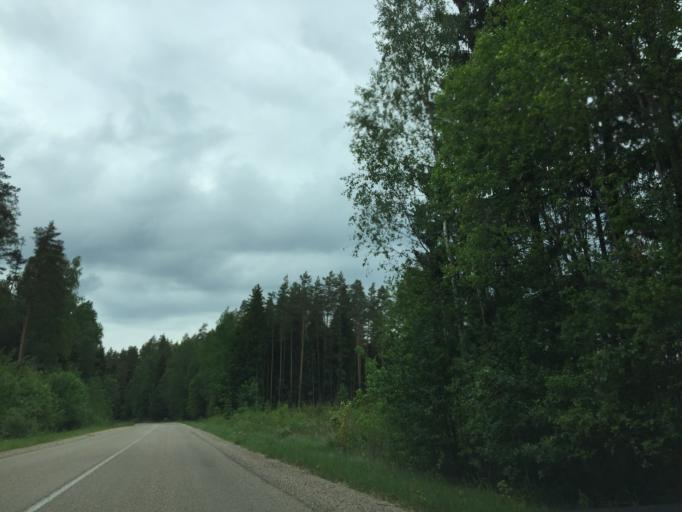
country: LV
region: Varkava
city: Vecvarkava
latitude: 56.0761
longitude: 26.6271
